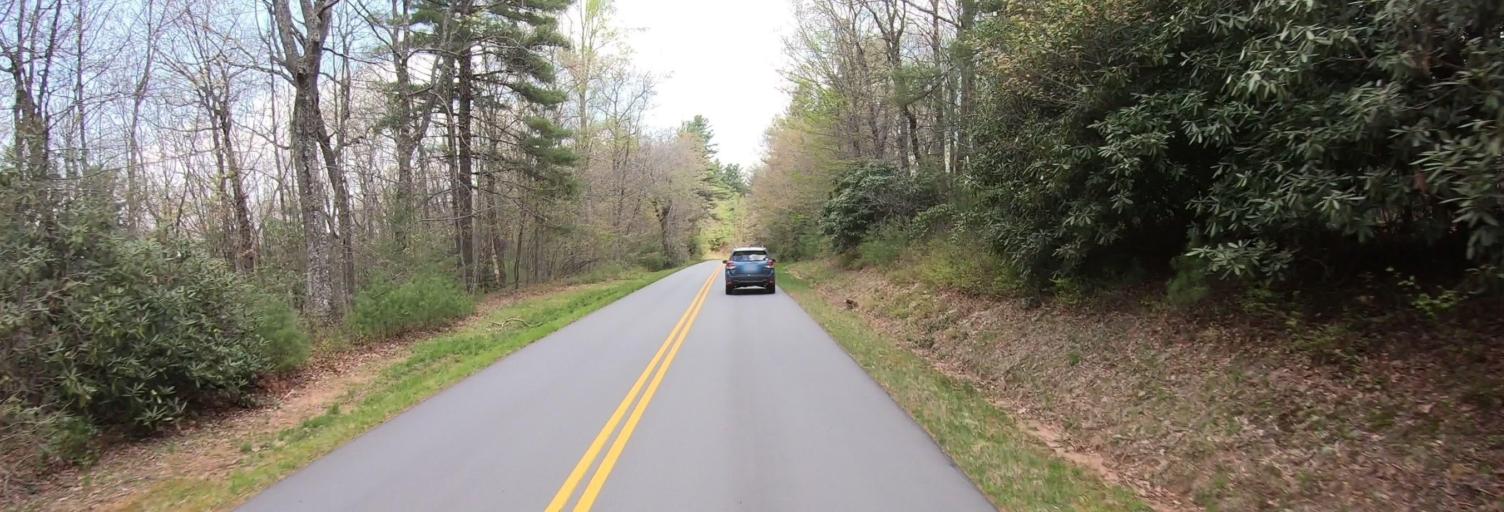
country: US
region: Virginia
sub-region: City of Galax
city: Galax
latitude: 36.5365
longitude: -80.9322
